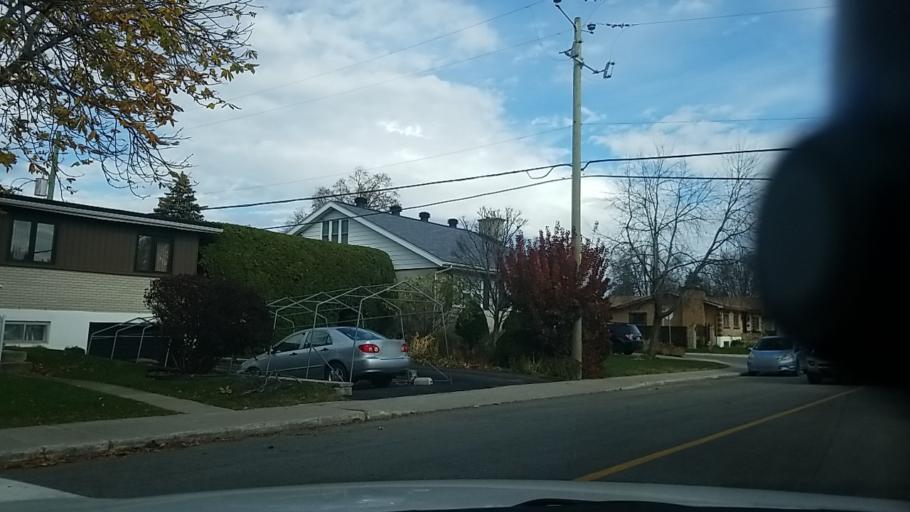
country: CA
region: Quebec
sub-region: Laval
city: Laval
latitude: 45.5759
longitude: -73.7315
